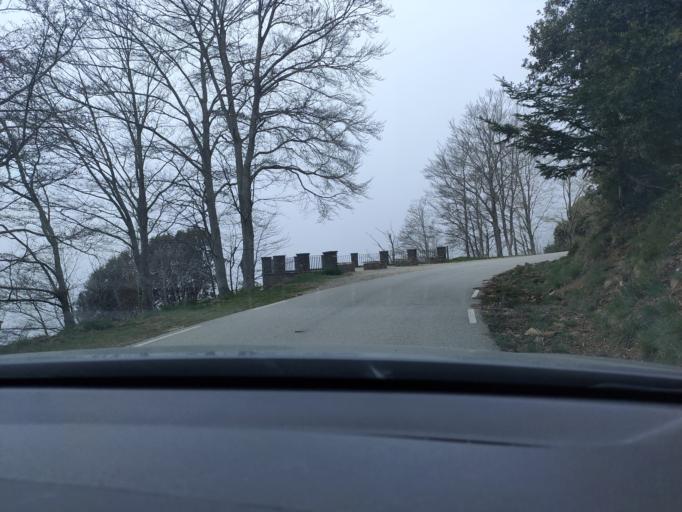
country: ES
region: Catalonia
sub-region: Provincia de Barcelona
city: Fogars de Montclus
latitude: 41.7572
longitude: 2.4523
